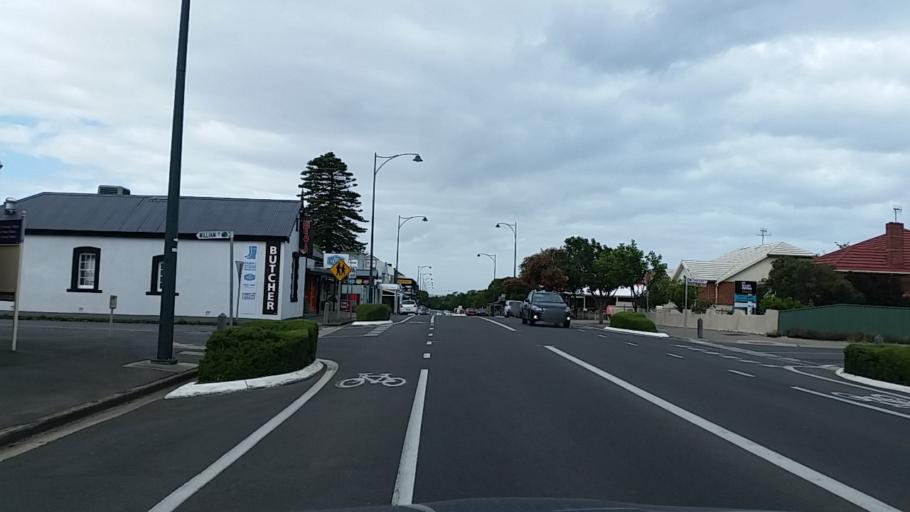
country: AU
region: South Australia
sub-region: Alexandrina
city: Port Elliot
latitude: -35.5305
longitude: 138.6797
